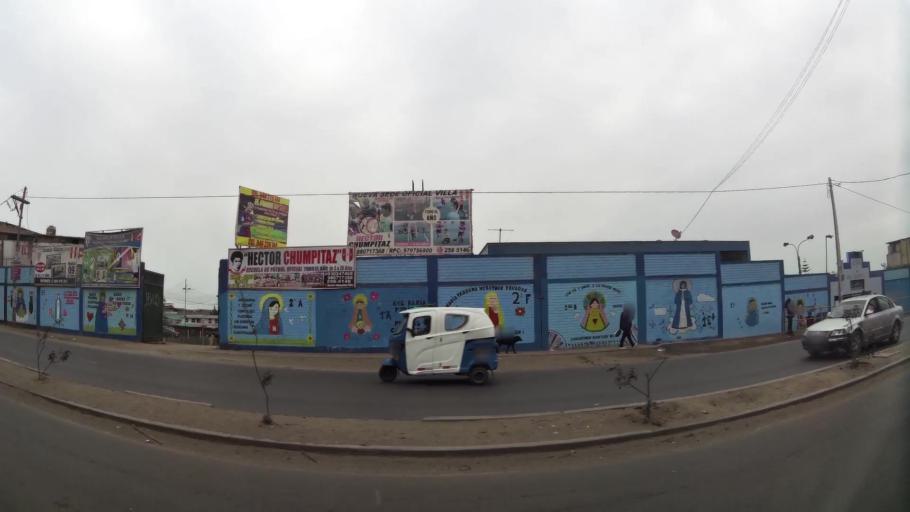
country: PE
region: Lima
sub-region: Lima
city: Surco
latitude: -12.2073
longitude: -76.9469
